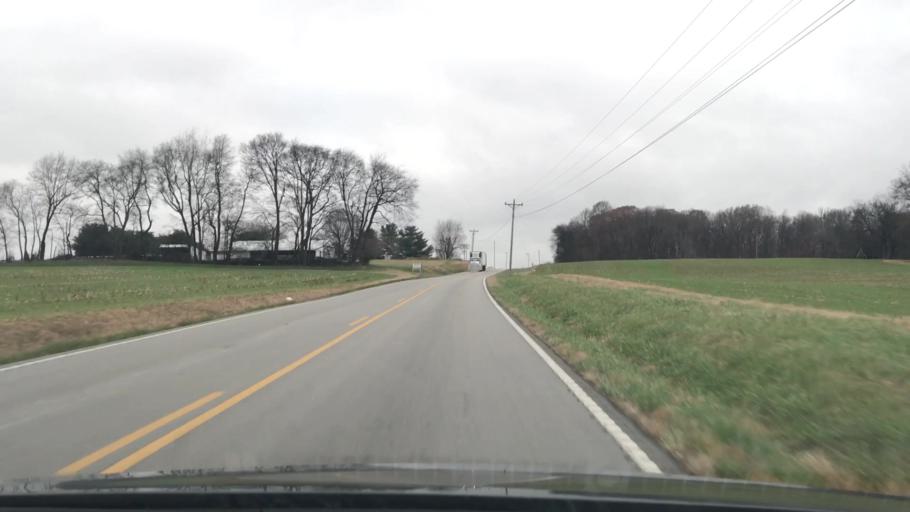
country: US
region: Kentucky
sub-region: Todd County
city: Guthrie
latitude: 36.6831
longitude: -87.2006
